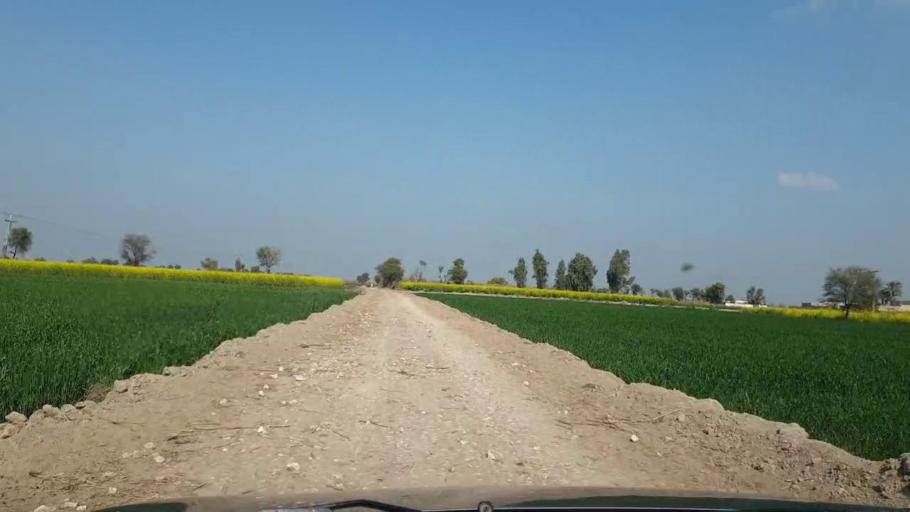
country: PK
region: Sindh
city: Sinjhoro
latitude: 26.0534
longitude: 68.7294
